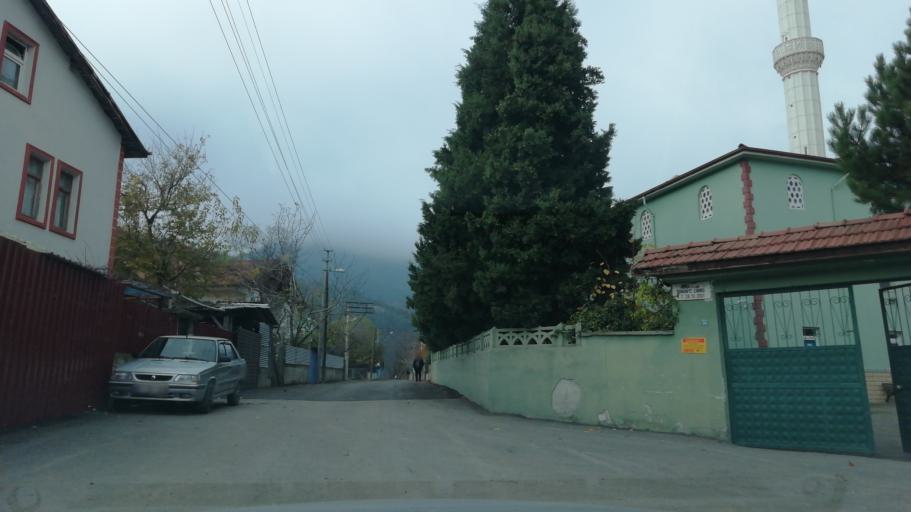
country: TR
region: Karabuk
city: Karabuk
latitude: 41.2298
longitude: 32.6204
